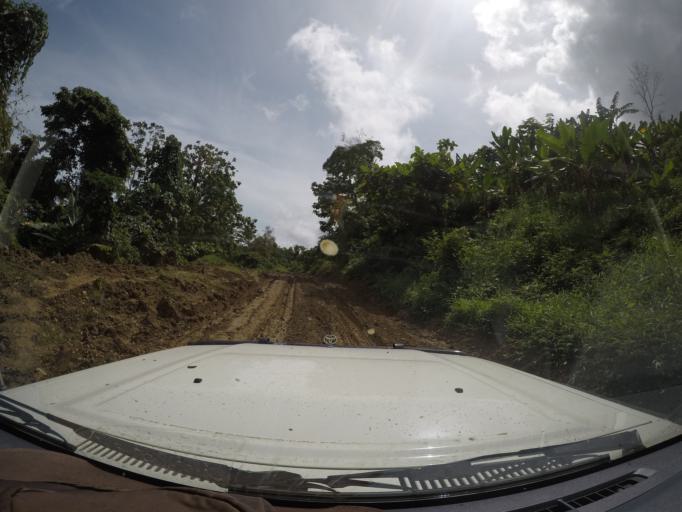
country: PG
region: Gulf
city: Kerema
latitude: -7.9912
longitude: 145.8311
